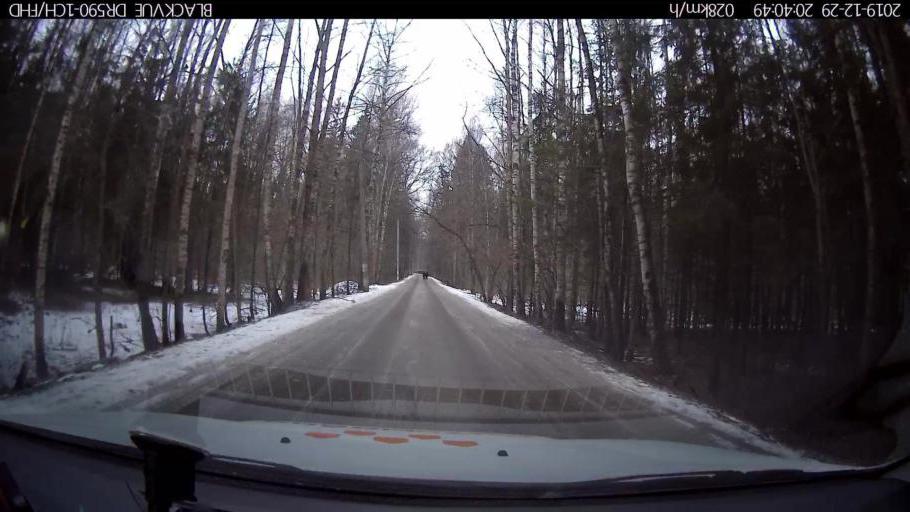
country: RU
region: Nizjnij Novgorod
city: Afonino
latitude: 56.1889
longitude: 44.0416
